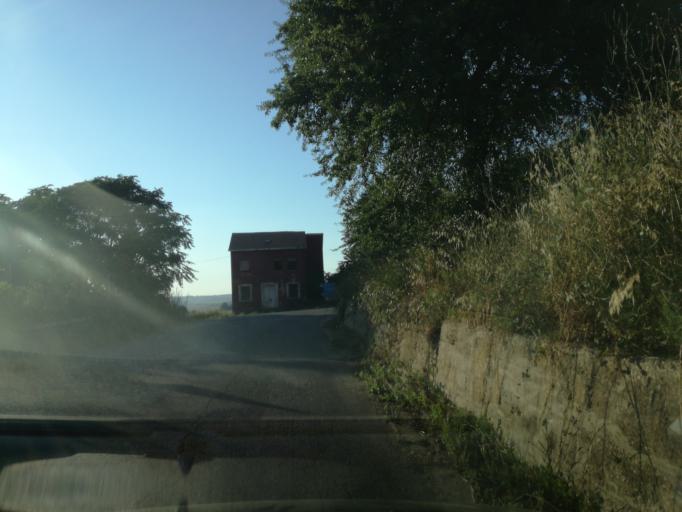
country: IT
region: Molise
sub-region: Provincia di Campobasso
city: Guglionesi
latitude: 41.9325
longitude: 14.9414
